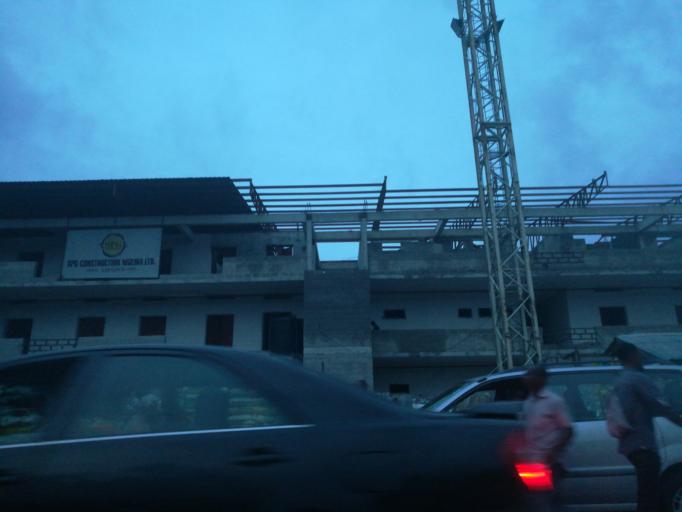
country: NG
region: Rivers
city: Port Harcourt
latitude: 4.7914
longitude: 6.9986
